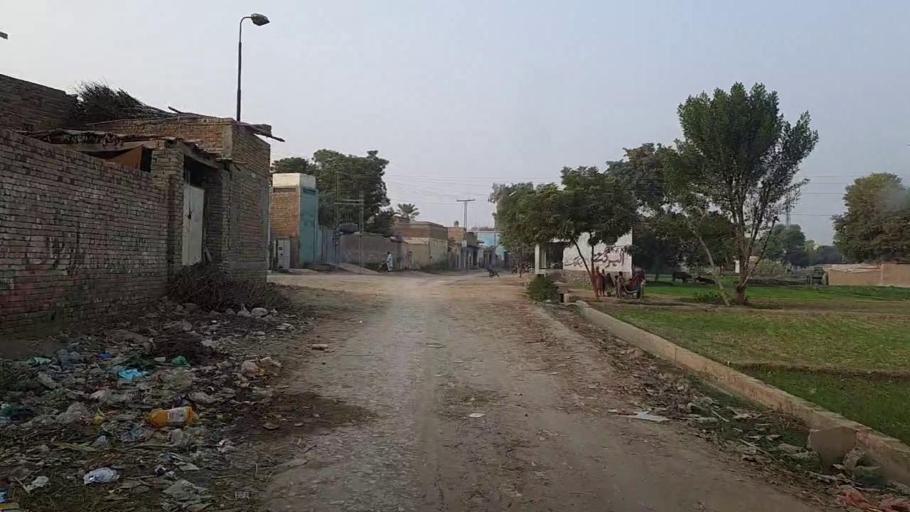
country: PK
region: Sindh
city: Setharja Old
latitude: 27.0848
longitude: 68.4956
